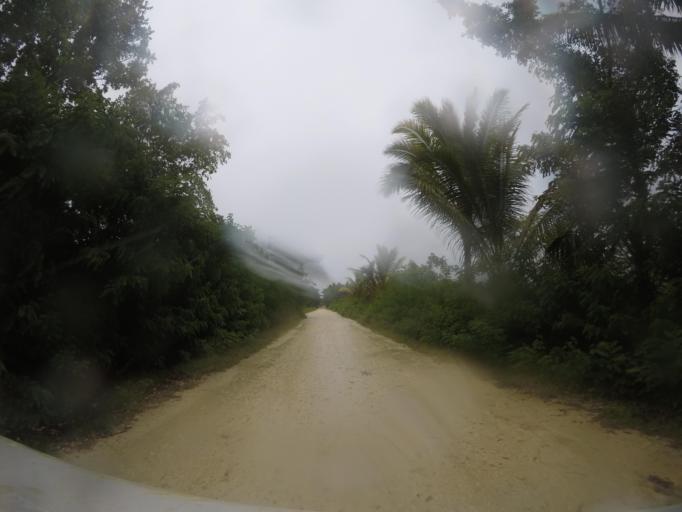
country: TL
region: Lautem
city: Lospalos
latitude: -8.5012
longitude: 127.0026
